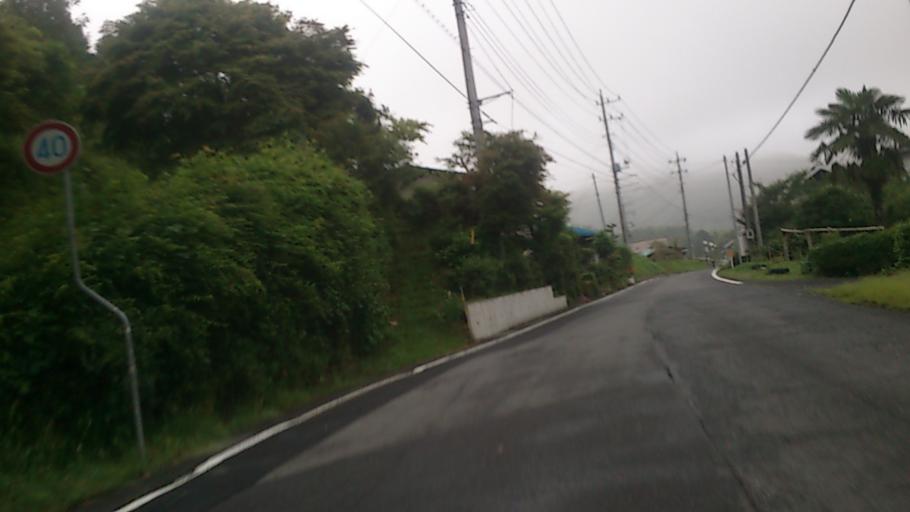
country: JP
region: Ibaraki
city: Daigo
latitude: 36.6661
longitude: 140.3131
